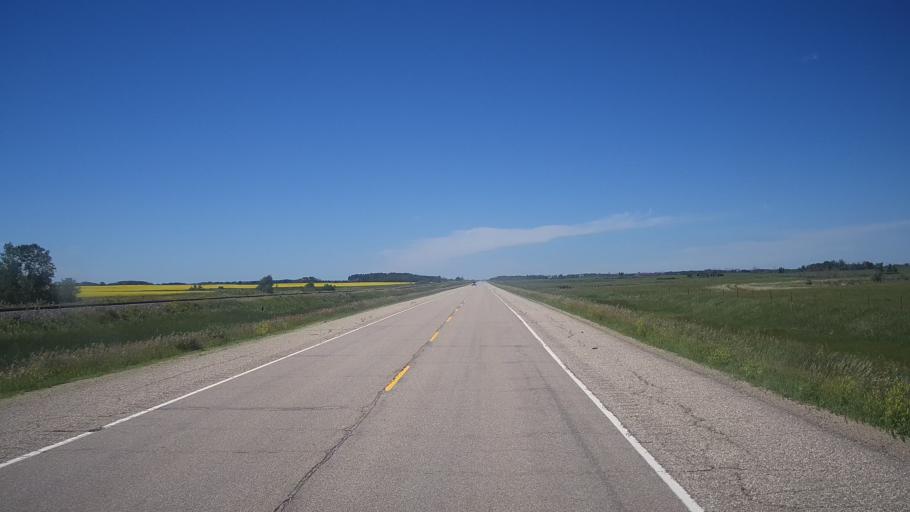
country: CA
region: Manitoba
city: Rivers
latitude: 50.4205
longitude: -100.4903
